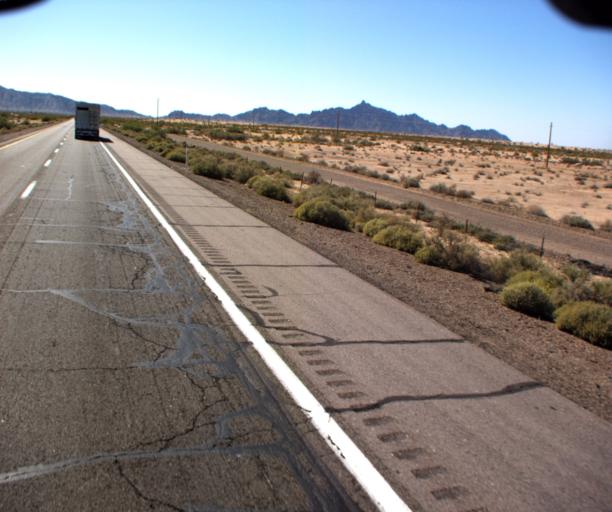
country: US
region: Arizona
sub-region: Yuma County
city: Wellton
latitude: 32.7498
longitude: -113.6648
